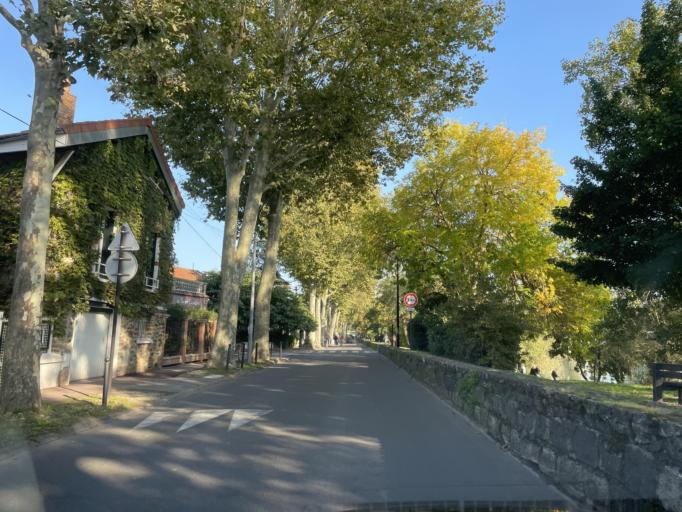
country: FR
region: Ile-de-France
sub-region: Departement du Val-de-Marne
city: Saint-Maur-des-Fosses
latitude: 48.7850
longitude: 2.5023
